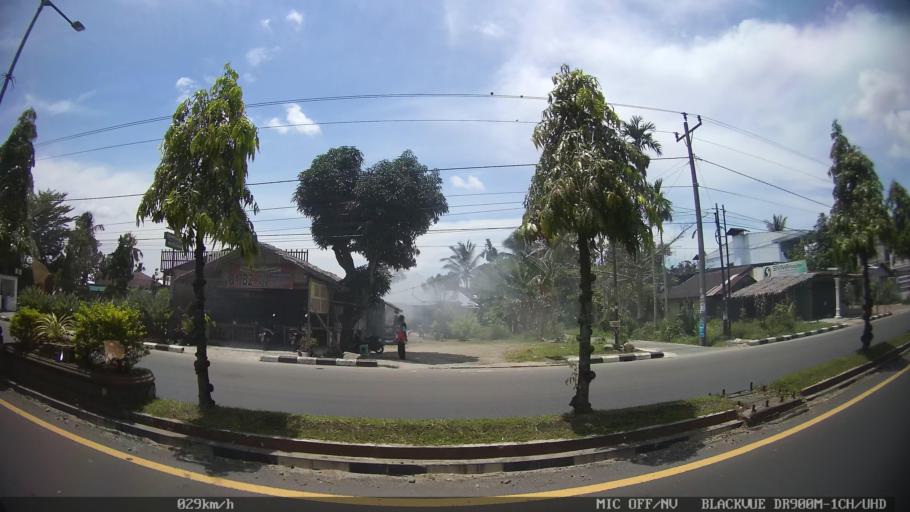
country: ID
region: North Sumatra
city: Binjai
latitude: 3.6086
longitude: 98.5038
